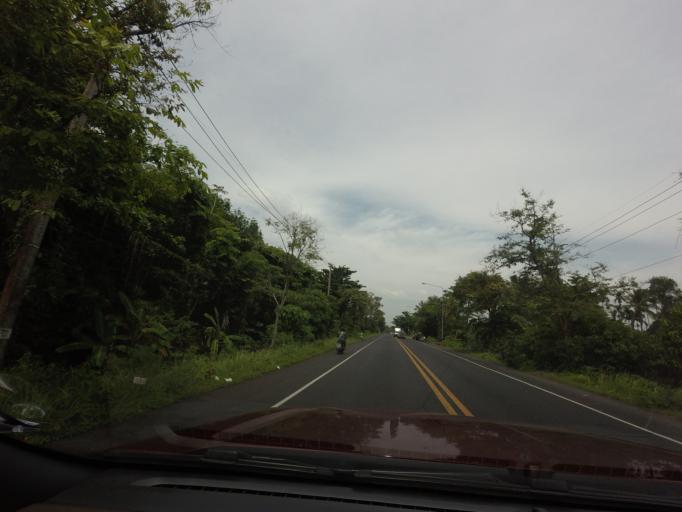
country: TH
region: Pattani
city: Mae Lan
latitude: 6.6406
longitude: 101.3028
